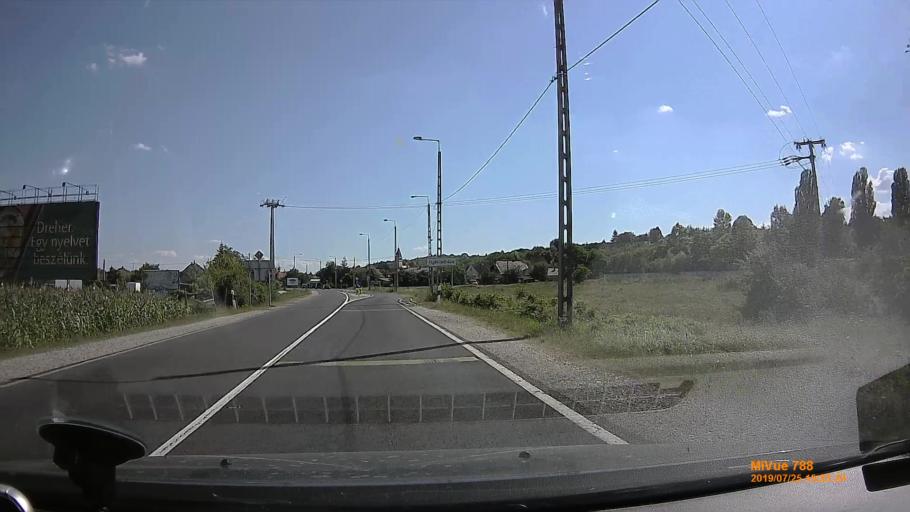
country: HU
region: Borsod-Abauj-Zemplen
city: Nyekladhaza
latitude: 47.9947
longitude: 20.8305
